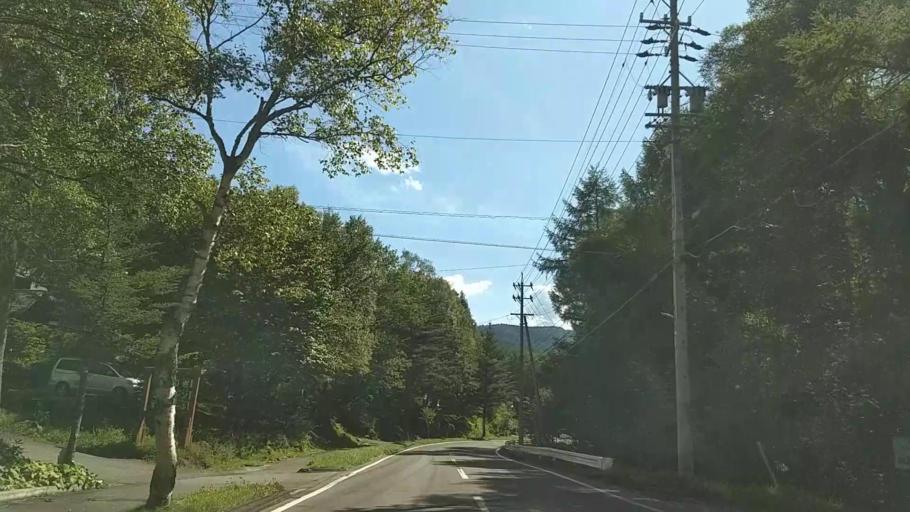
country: JP
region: Nagano
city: Chino
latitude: 36.1198
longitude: 138.2620
